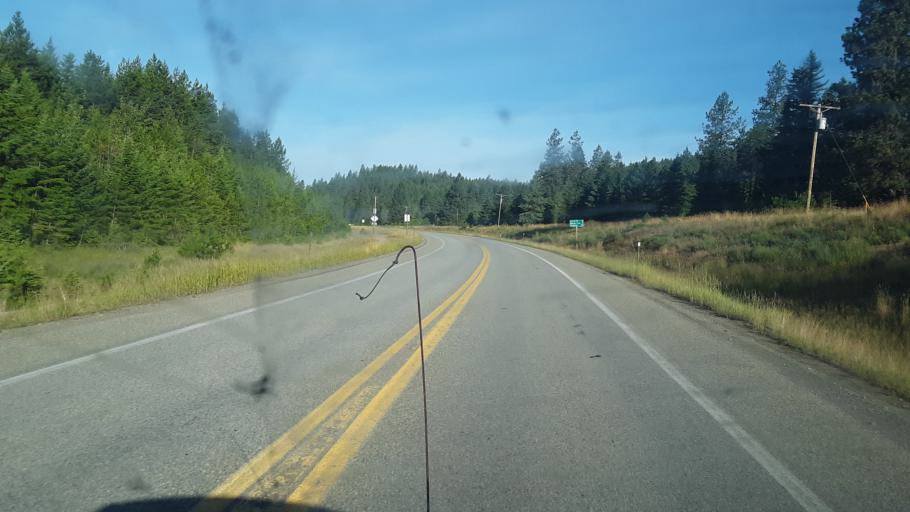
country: US
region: Idaho
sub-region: Boundary County
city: Bonners Ferry
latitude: 48.7323
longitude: -116.1847
